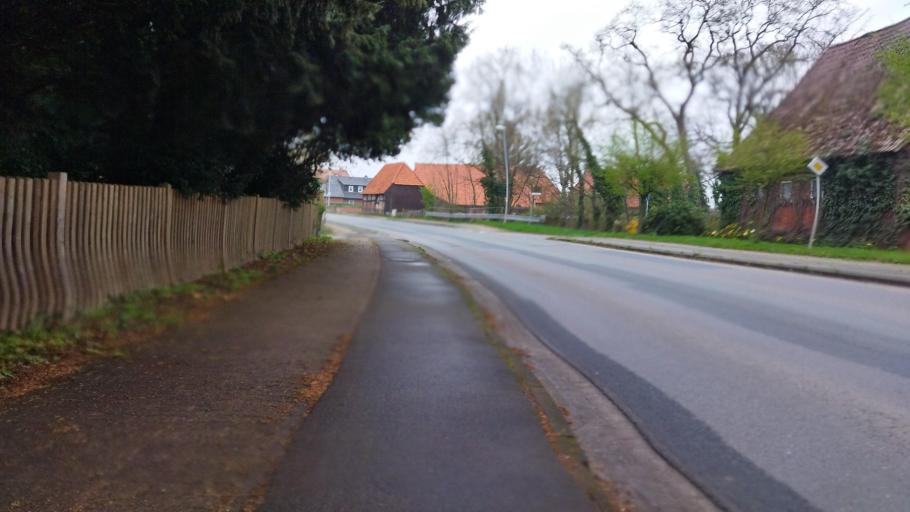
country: DE
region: Lower Saxony
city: Schweringen
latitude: 52.7295
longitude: 9.1884
